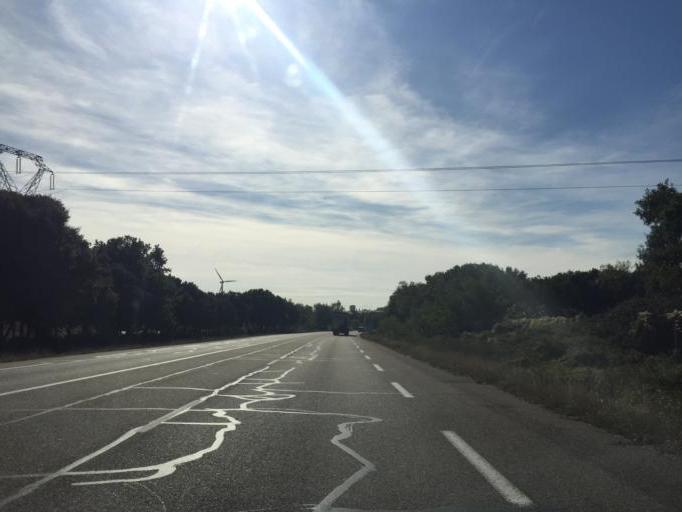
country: FR
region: Rhone-Alpes
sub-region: Departement de la Drome
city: Malataverne
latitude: 44.4554
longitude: 4.7519
